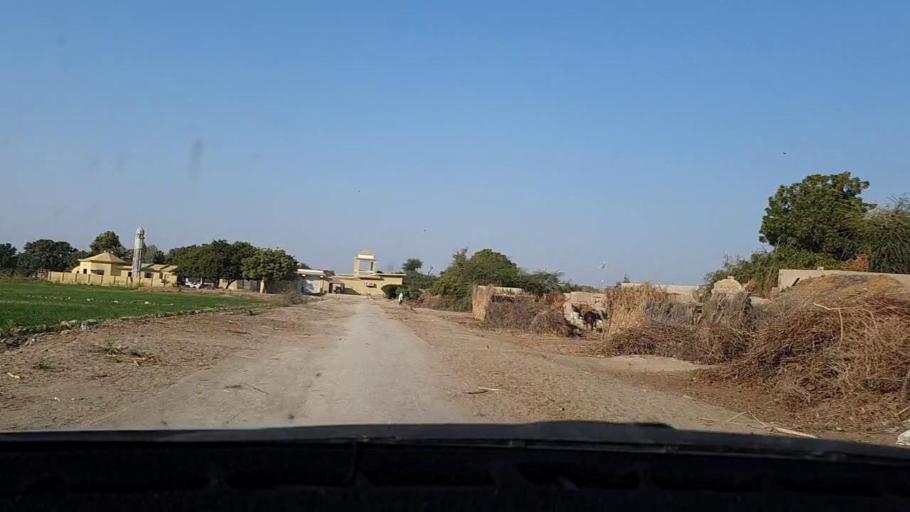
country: PK
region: Sindh
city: Tando Mittha Khan
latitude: 25.8568
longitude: 69.3334
